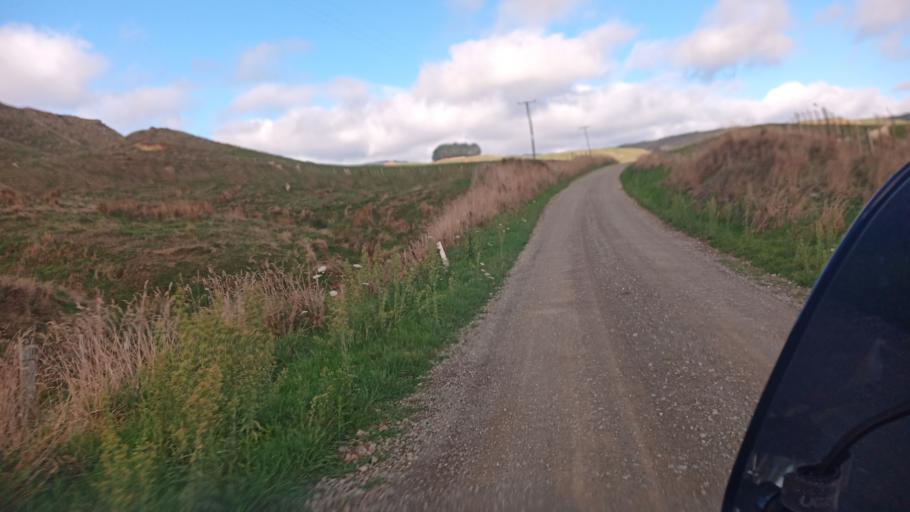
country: NZ
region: Bay of Plenty
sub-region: Opotiki District
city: Opotiki
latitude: -38.4568
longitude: 177.3923
